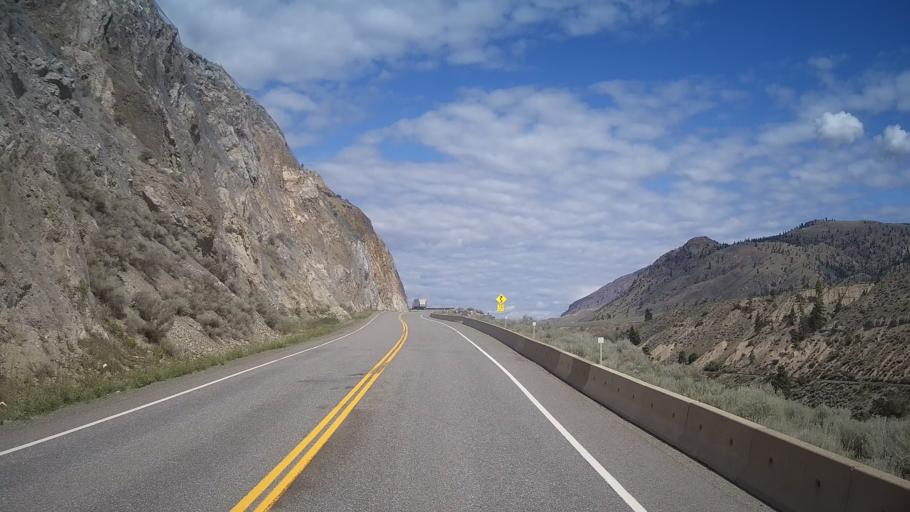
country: CA
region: British Columbia
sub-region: Thompson-Nicola Regional District
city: Ashcroft
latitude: 50.5358
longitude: -121.2861
